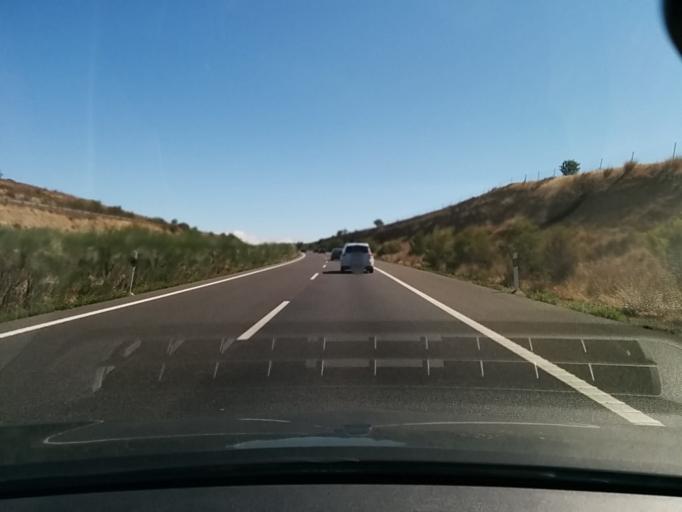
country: ES
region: Aragon
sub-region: Provincia de Huesca
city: Almudebar
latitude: 42.0593
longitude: -0.5335
